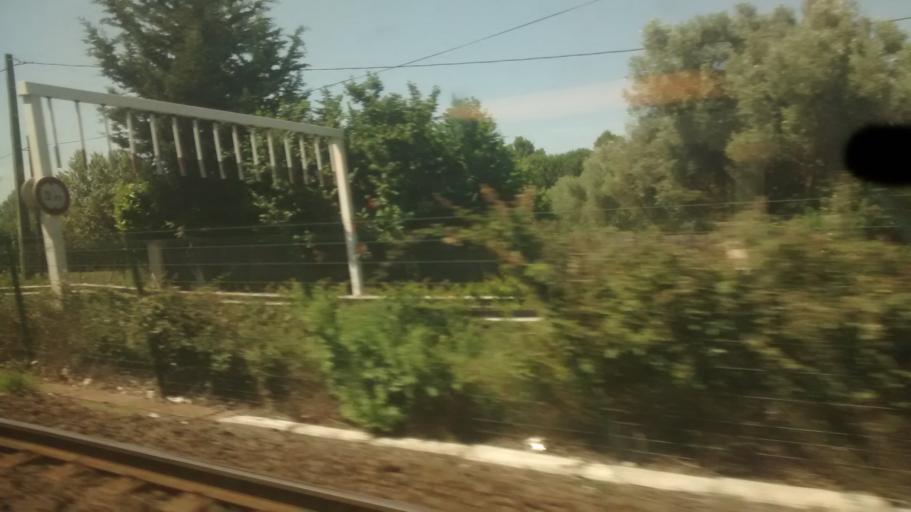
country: FR
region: Languedoc-Roussillon
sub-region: Departement de l'Herault
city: Lunel-Viel
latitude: 43.6819
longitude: 4.1086
